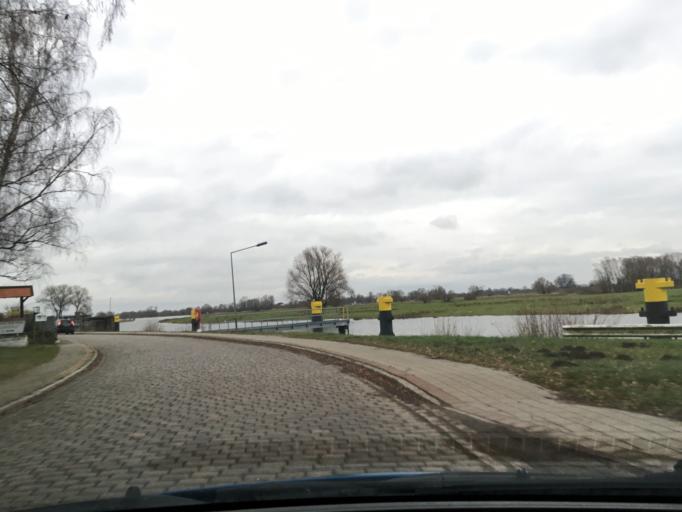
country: DE
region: Lower Saxony
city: Bleckede
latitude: 53.2935
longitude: 10.7355
